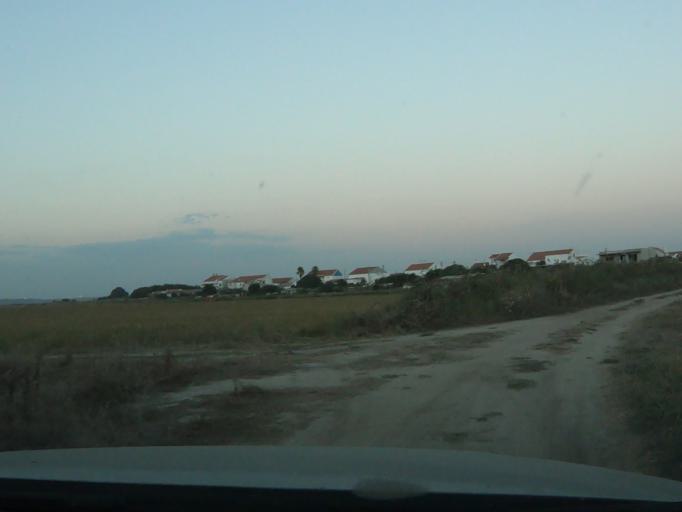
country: PT
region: Setubal
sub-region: Setubal
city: Setubal
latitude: 38.4098
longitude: -8.7559
